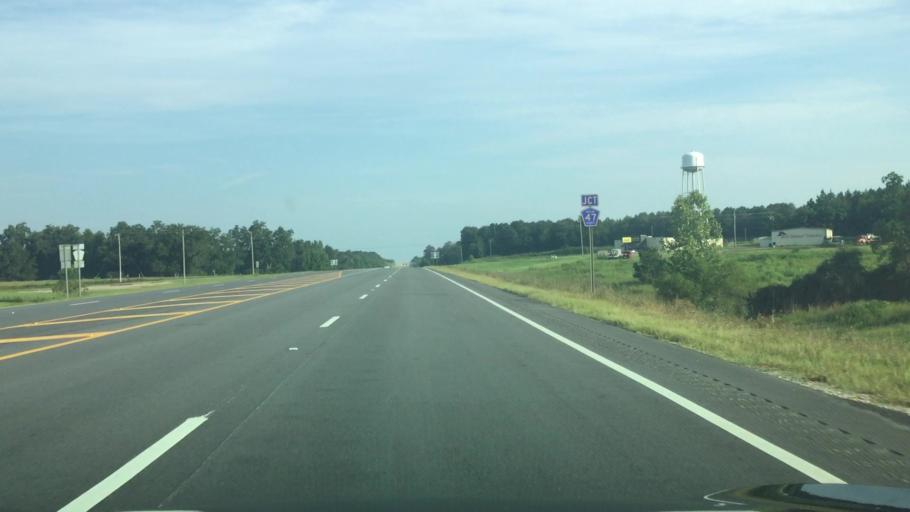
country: US
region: Alabama
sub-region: Butler County
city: Georgiana
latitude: 31.5291
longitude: -86.7198
